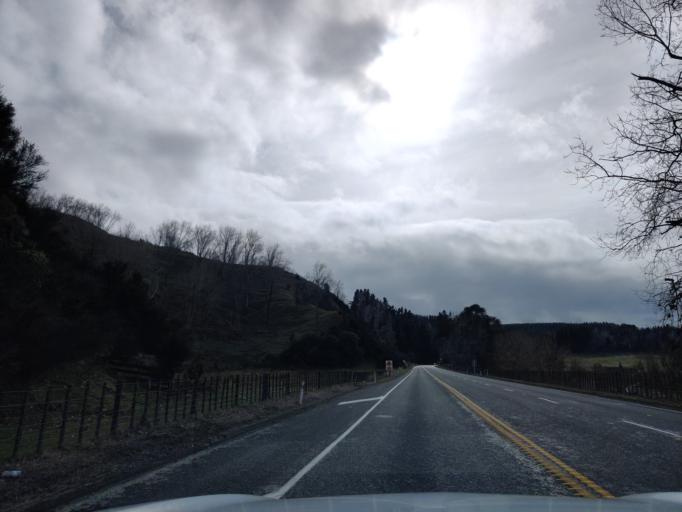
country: NZ
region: Manawatu-Wanganui
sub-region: Ruapehu District
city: Waiouru
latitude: -39.7651
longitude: 175.8017
